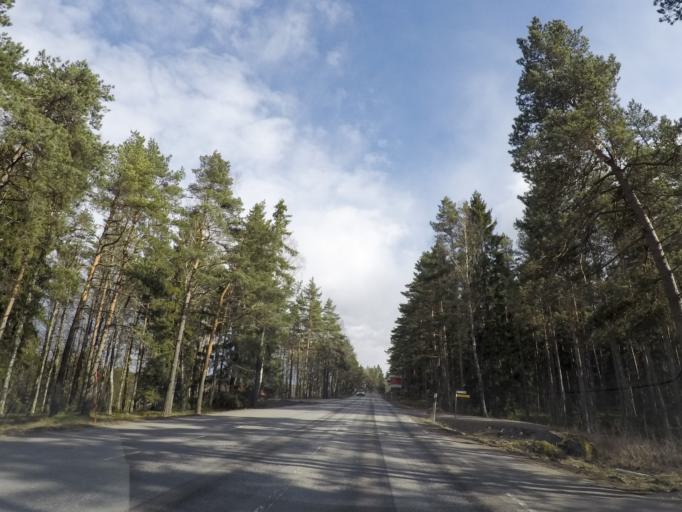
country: SE
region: Vaestmanland
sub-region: Hallstahammars Kommun
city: Hallstahammar
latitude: 59.6428
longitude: 16.1938
